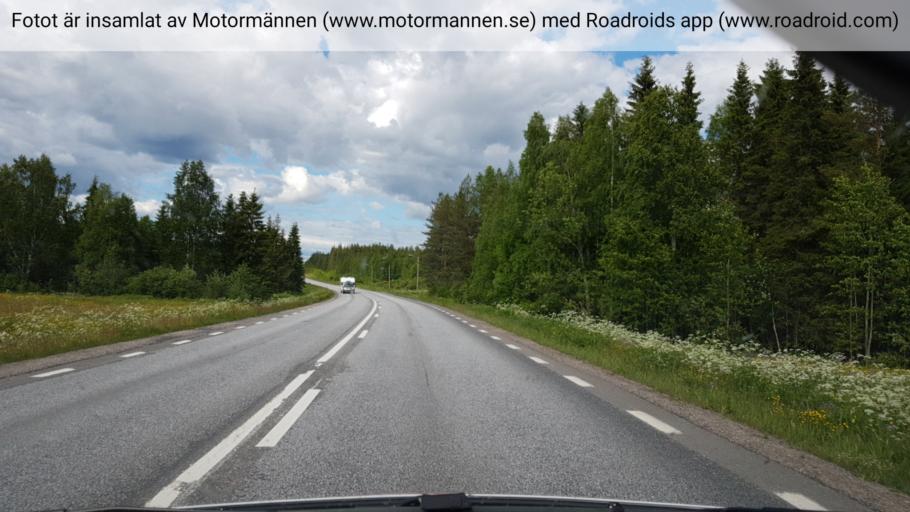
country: SE
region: Norrbotten
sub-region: Kalix Kommun
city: Toere
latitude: 66.0809
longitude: 22.7143
